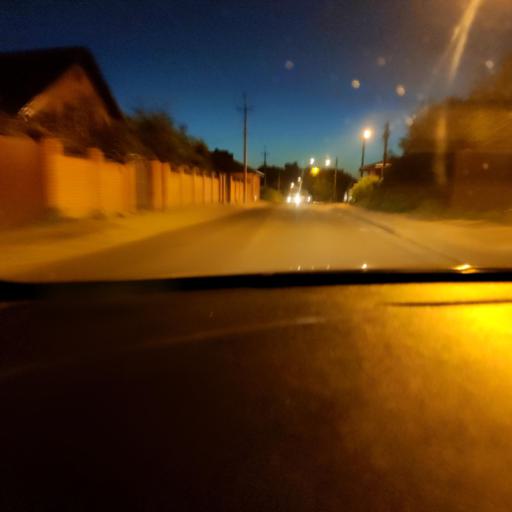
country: RU
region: Tatarstan
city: Vysokaya Gora
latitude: 55.8642
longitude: 49.2370
